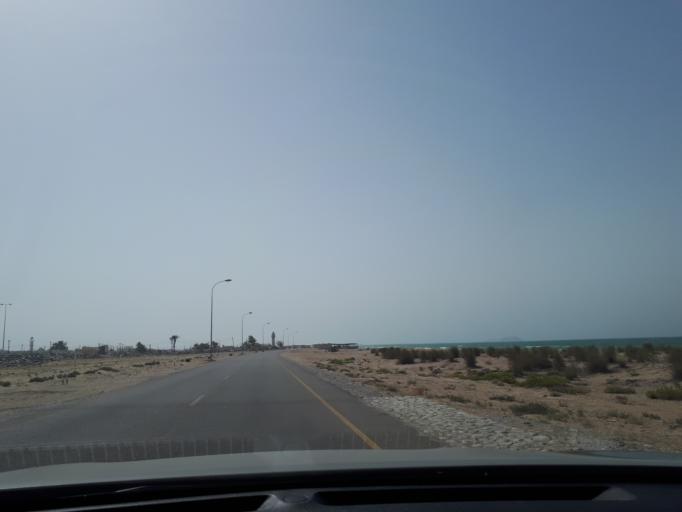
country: OM
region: Al Batinah
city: Barka'
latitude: 23.7176
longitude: 57.8615
